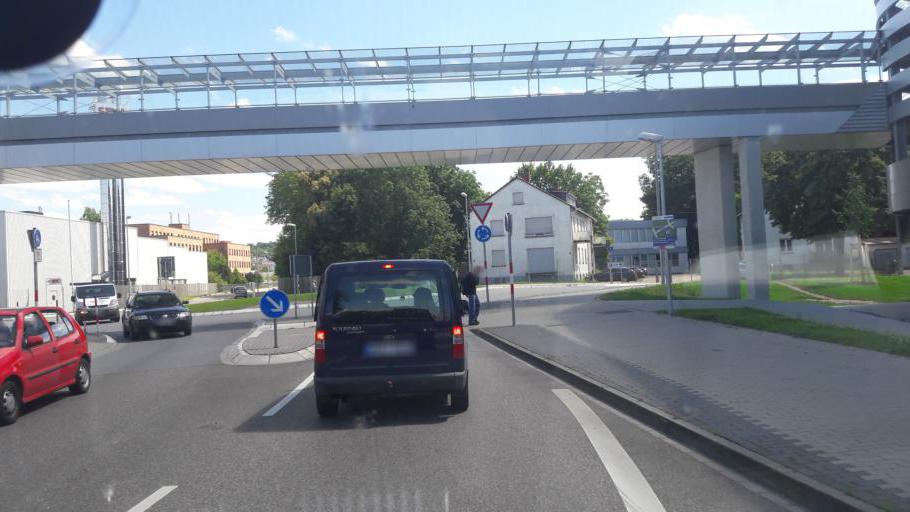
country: DE
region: Baden-Wuerttemberg
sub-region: Karlsruhe Region
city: Bruchsal
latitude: 49.1229
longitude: 8.5759
